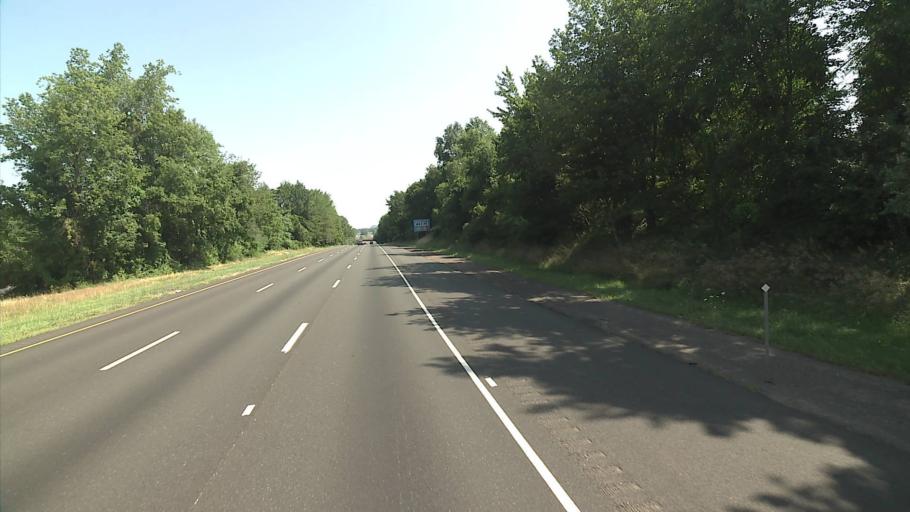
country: US
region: Connecticut
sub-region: New Haven County
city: Wallingford Center
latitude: 41.4622
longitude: -72.7766
